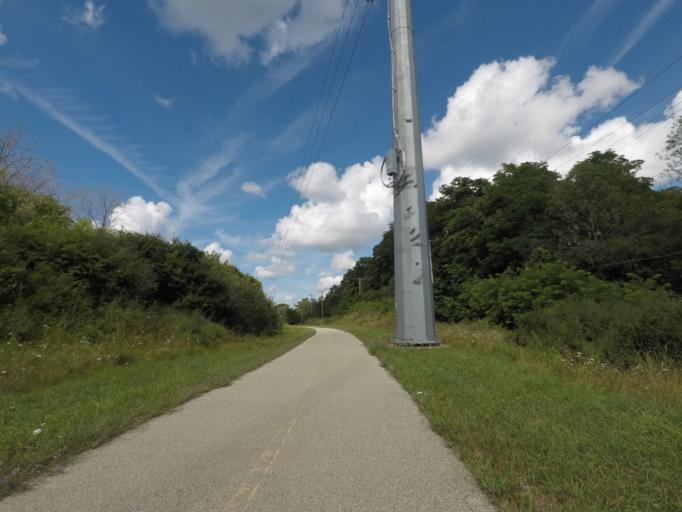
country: US
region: Wisconsin
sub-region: Waukesha County
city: Pewaukee
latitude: 43.0606
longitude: -88.2995
